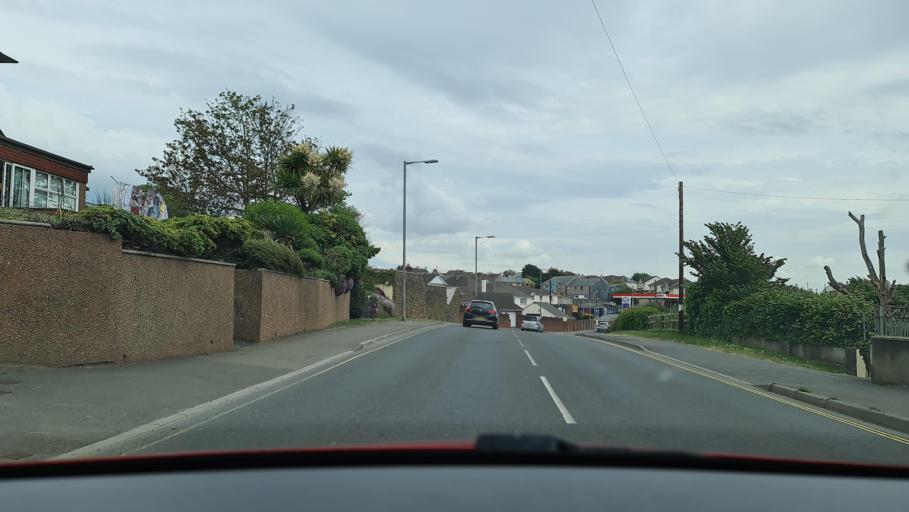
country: GB
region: England
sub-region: Cornwall
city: Bude
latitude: 50.8261
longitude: -4.5430
